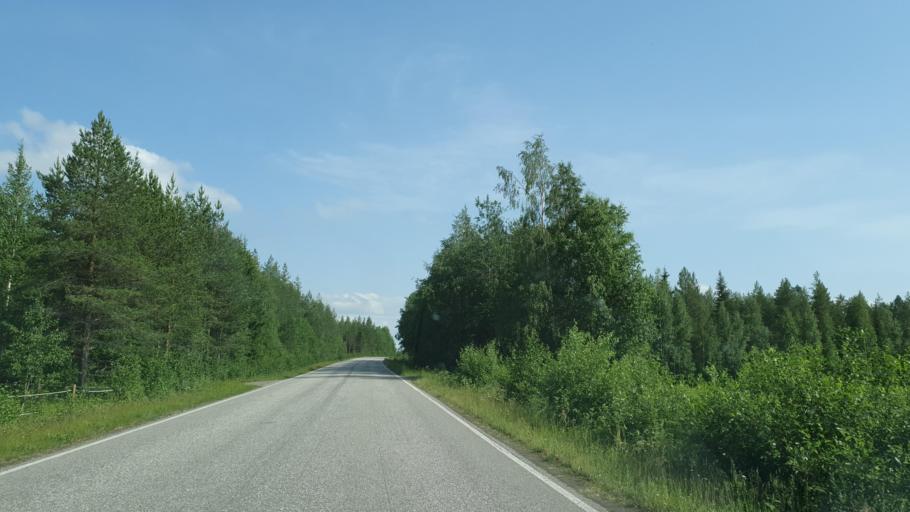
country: FI
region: Kainuu
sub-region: Kehys-Kainuu
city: Kuhmo
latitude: 64.1017
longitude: 29.7646
